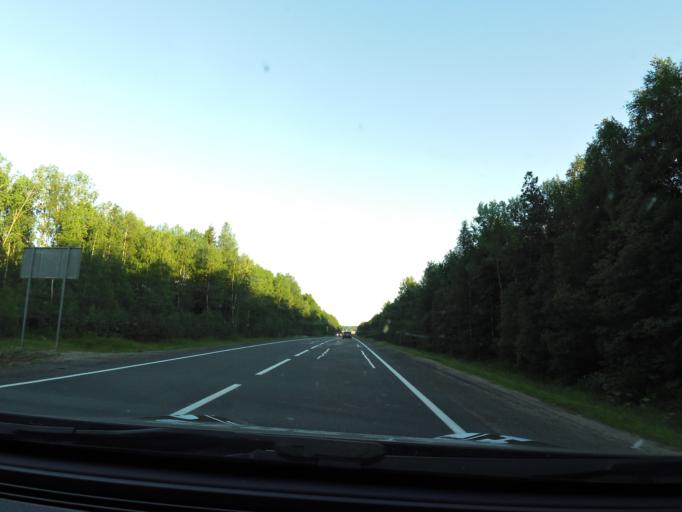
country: RU
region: Vologda
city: Gryazovets
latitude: 58.7611
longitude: 40.2805
